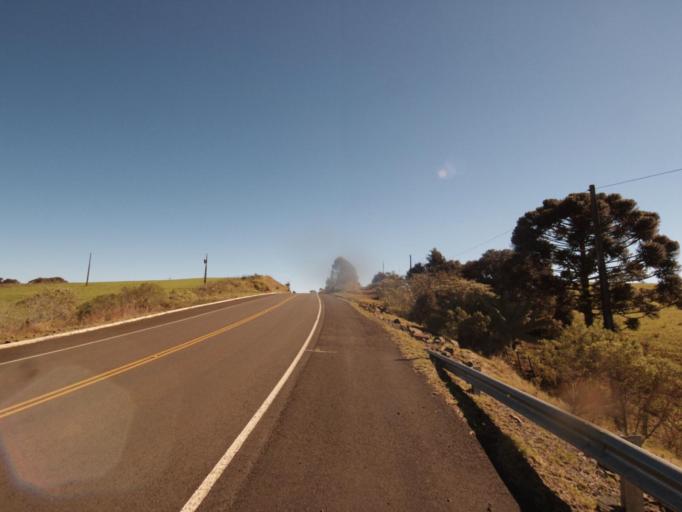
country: AR
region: Misiones
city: Bernardo de Irigoyen
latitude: -26.6696
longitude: -53.5940
